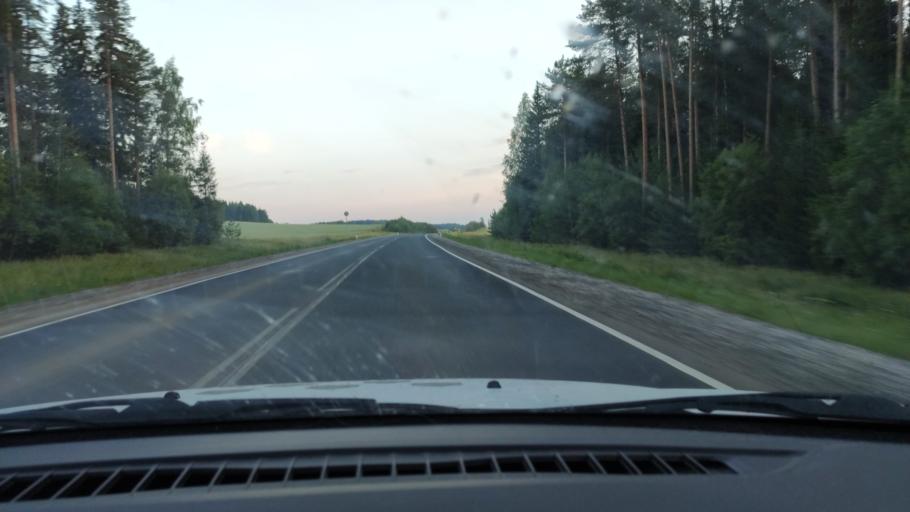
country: RU
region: Perm
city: Siva
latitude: 58.4129
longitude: 54.4681
